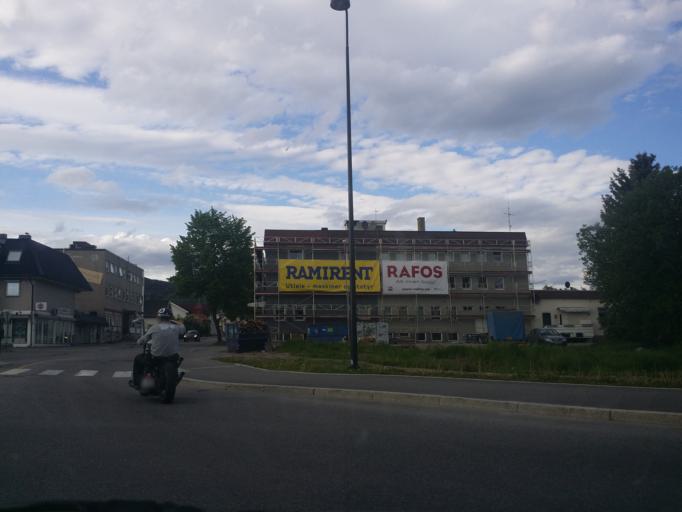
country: NO
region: Hedmark
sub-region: Ringsaker
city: Brumunddal
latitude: 60.8862
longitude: 10.9402
